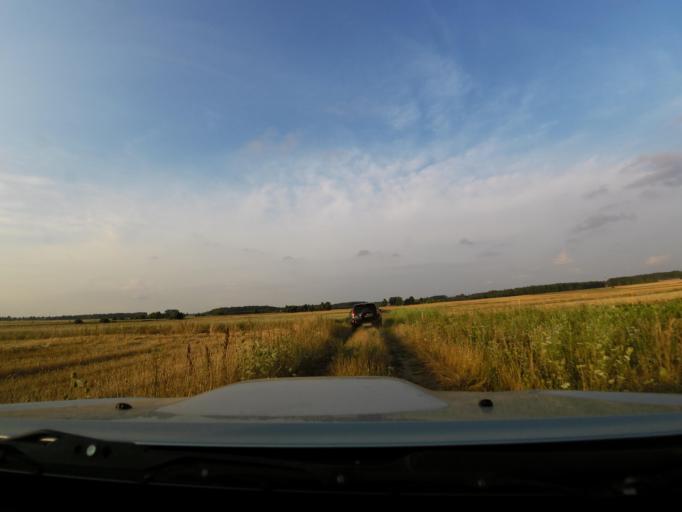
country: LT
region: Klaipedos apskritis
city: Silute
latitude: 55.4700
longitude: 21.4622
